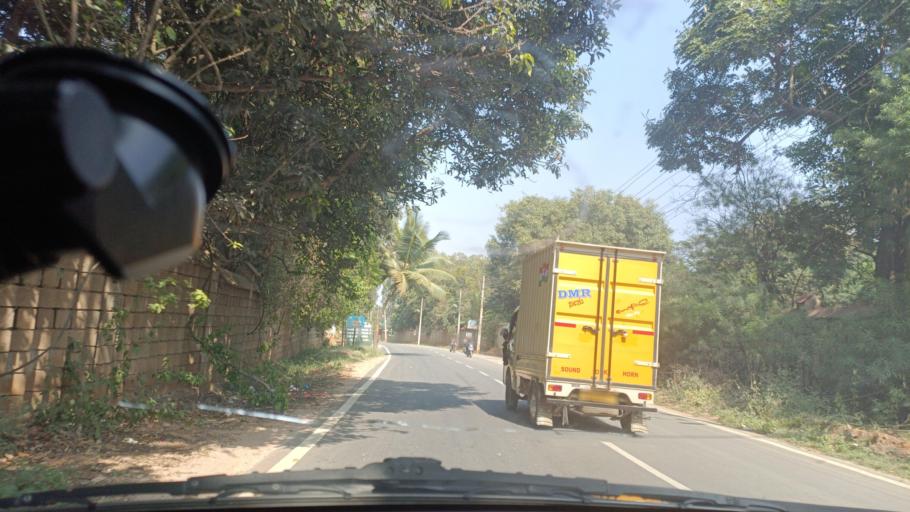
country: IN
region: Karnataka
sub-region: Bangalore Rural
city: Devanhalli
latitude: 13.2037
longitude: 77.6455
